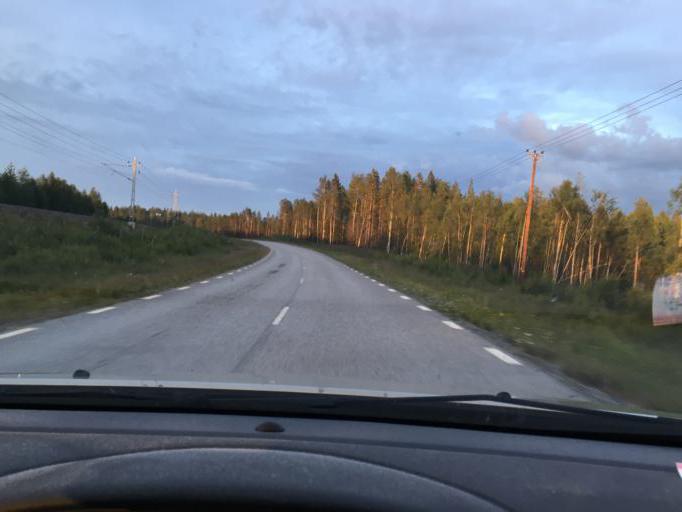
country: SE
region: Norrbotten
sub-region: Lulea Kommun
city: Ranea
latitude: 66.0396
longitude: 22.3245
